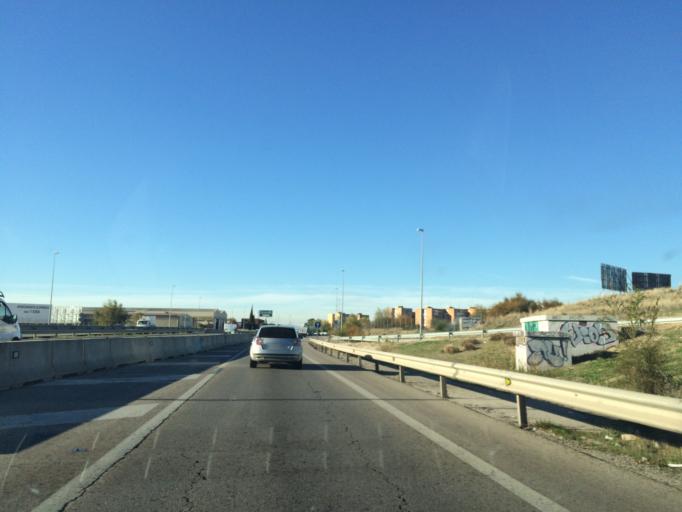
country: ES
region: Madrid
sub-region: Provincia de Madrid
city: Mostoles
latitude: 40.3083
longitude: -3.8338
